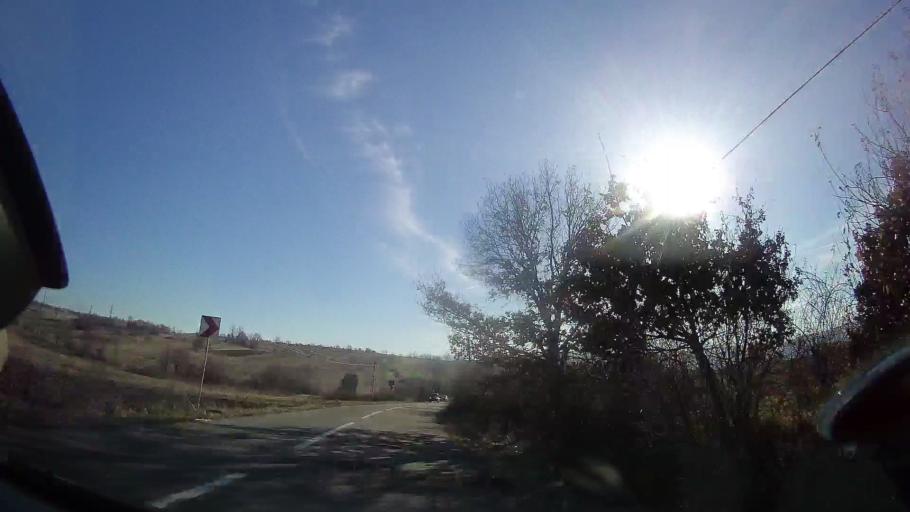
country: RO
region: Bihor
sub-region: Comuna Suncuius
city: Balnaca
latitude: 46.9649
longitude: 22.5522
